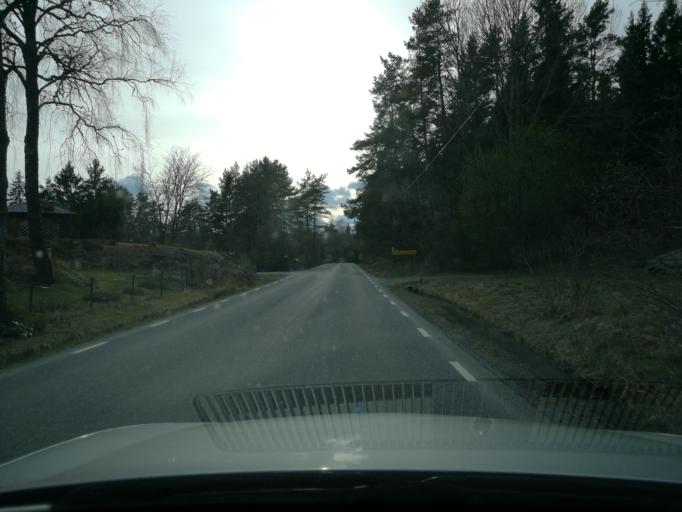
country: SE
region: Soedermanland
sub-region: Gnesta Kommun
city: Gnesta
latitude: 58.9824
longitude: 17.2930
